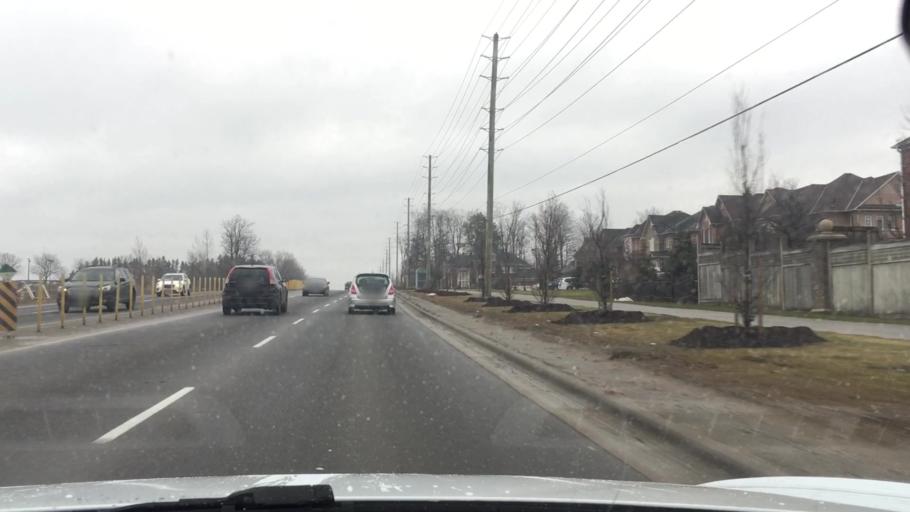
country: CA
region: Ontario
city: Ajax
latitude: 43.9113
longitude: -78.9718
